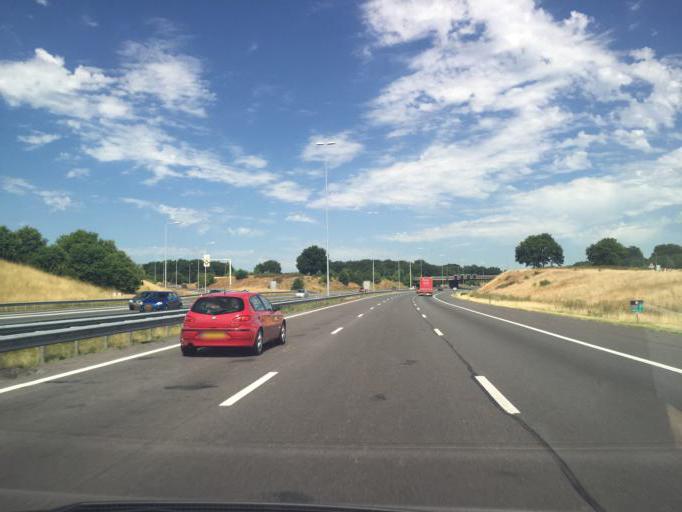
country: NL
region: Gelderland
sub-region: Gemeente Renkum
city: Heelsum
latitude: 51.9723
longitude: 5.7659
